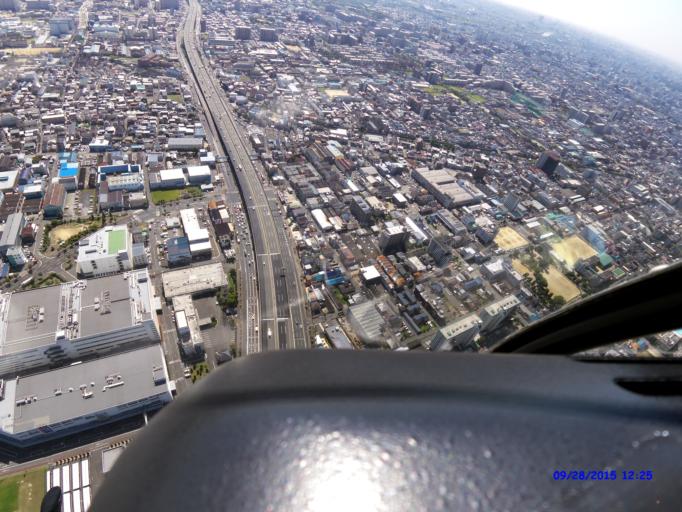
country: JP
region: Osaka
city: Yao
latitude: 34.6245
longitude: 135.5761
